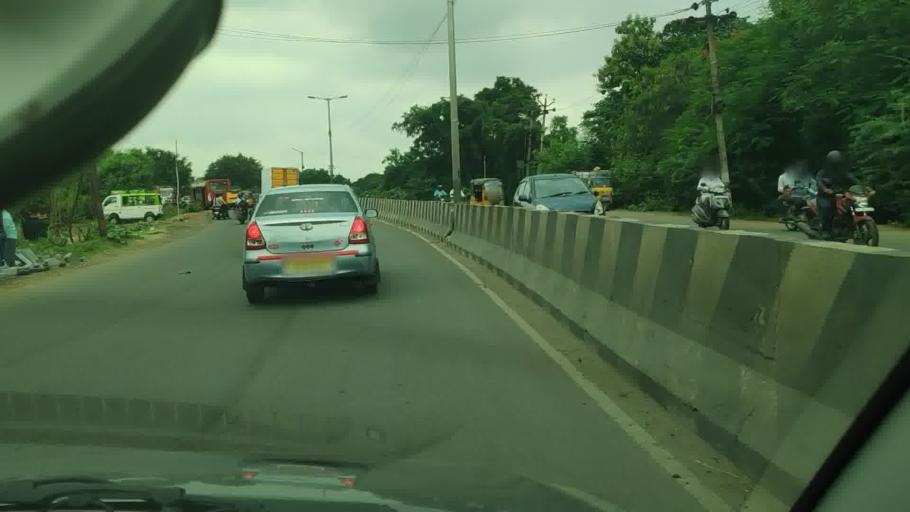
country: IN
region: Tamil Nadu
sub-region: Thiruvallur
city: Ambattur
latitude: 13.1156
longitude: 80.1479
